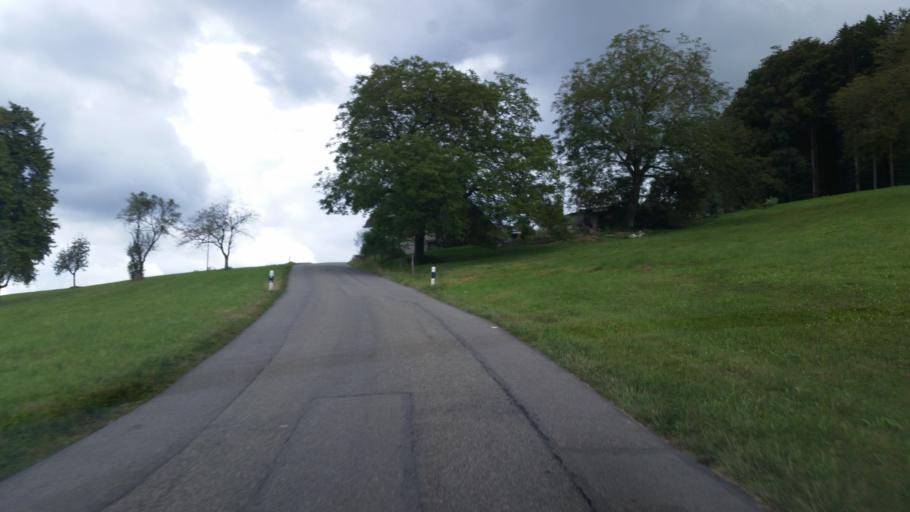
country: CH
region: Zurich
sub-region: Bezirk Affoltern
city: Hedingen
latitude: 47.3203
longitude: 8.4319
